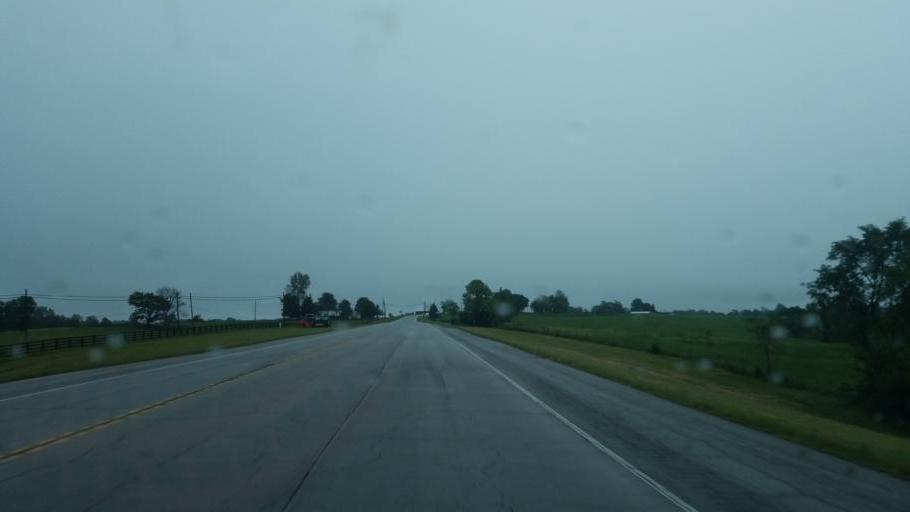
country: US
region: Kentucky
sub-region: Fleming County
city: Flemingsburg
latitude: 38.3962
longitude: -83.7052
